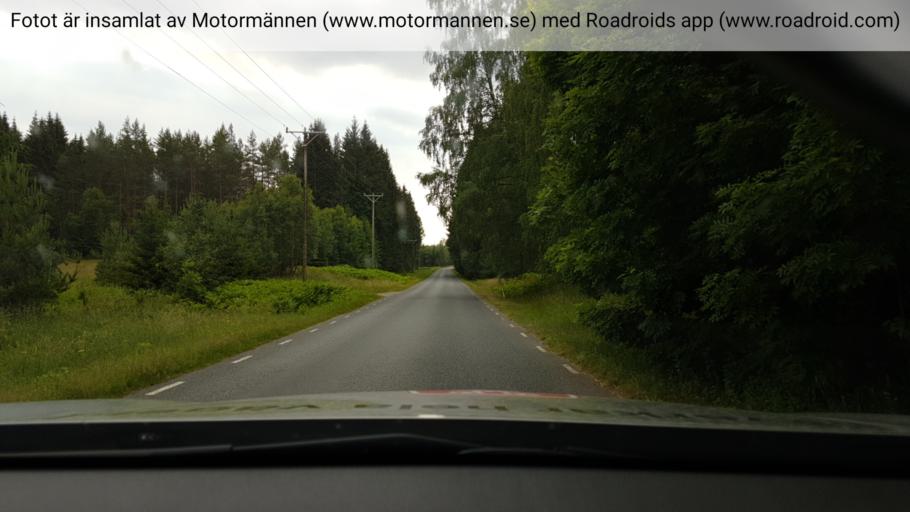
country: SE
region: Joenkoeping
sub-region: Habo Kommun
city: Habo
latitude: 58.0067
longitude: 14.0084
